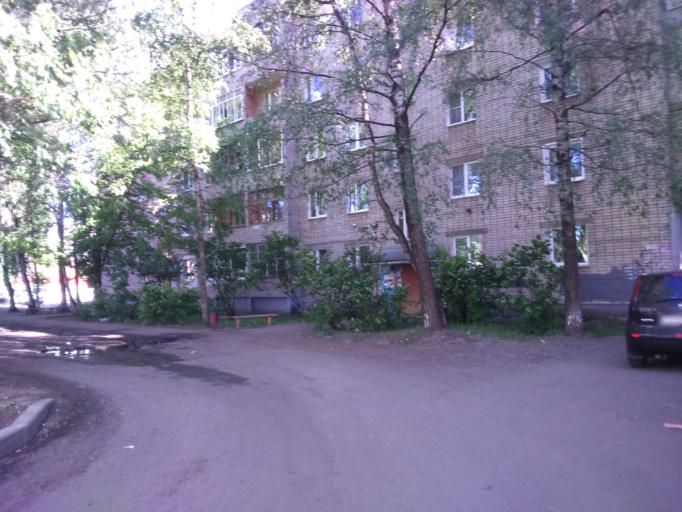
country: RU
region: Jaroslavl
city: Yaroslavl
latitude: 57.5793
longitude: 39.8568
